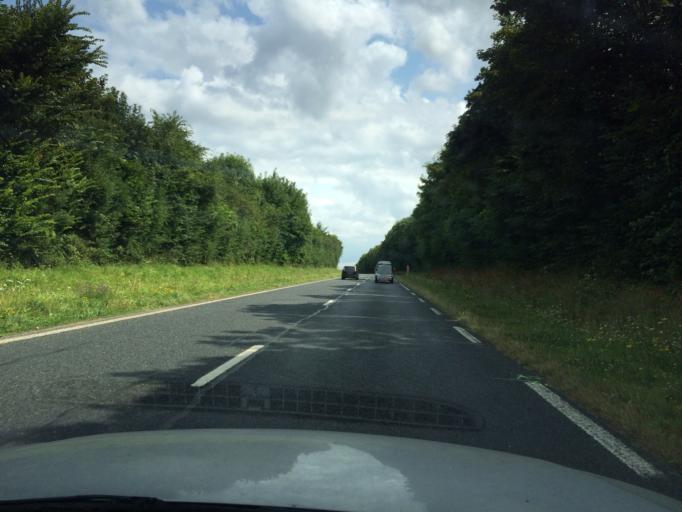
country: FR
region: Lower Normandy
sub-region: Departement du Calvados
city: Le Molay-Littry
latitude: 49.3271
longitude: -0.8815
